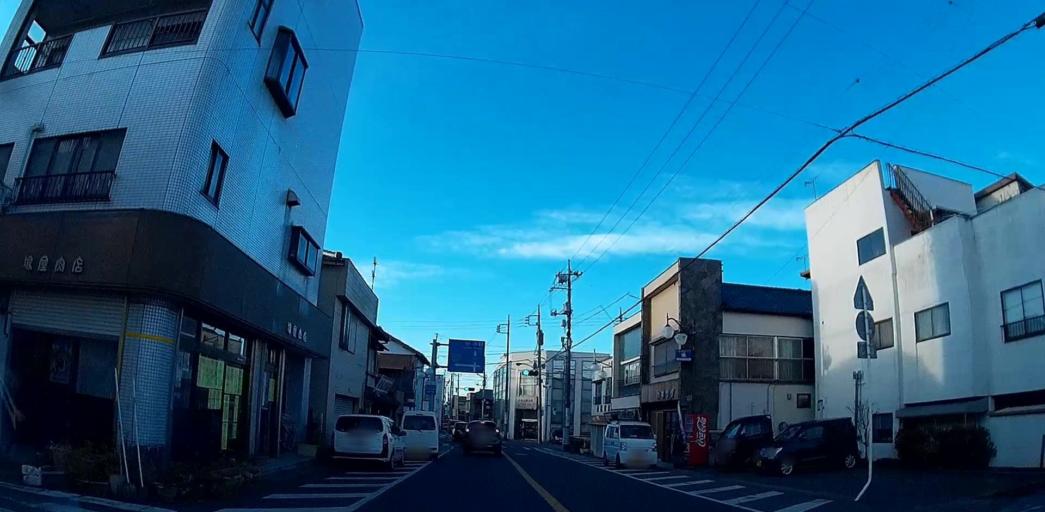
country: JP
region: Chiba
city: Omigawa
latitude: 35.8548
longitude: 140.6057
